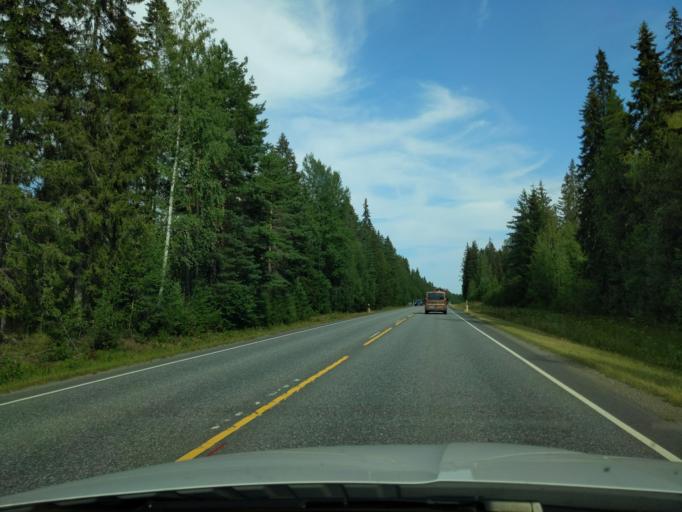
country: FI
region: Haeme
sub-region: Haemeenlinna
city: Hauho
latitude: 61.1736
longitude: 24.5939
